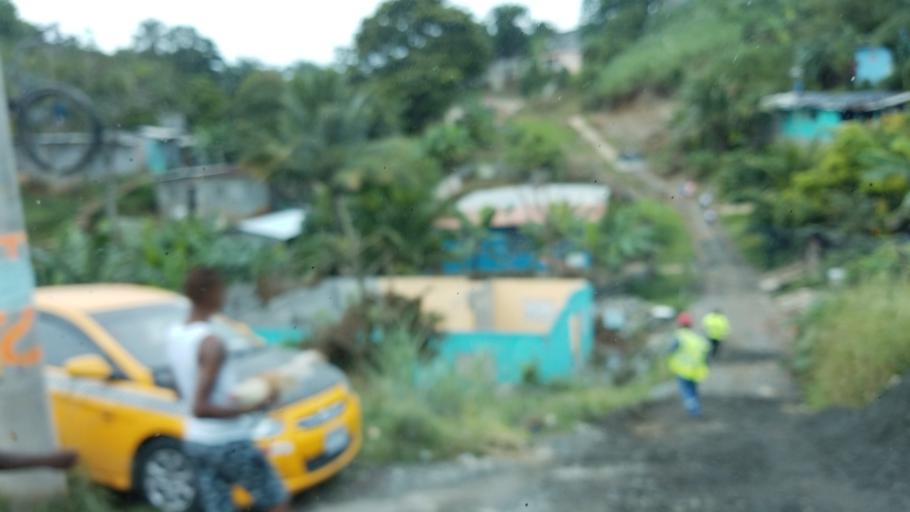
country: PA
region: Panama
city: Las Cumbres
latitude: 9.1021
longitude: -79.4956
